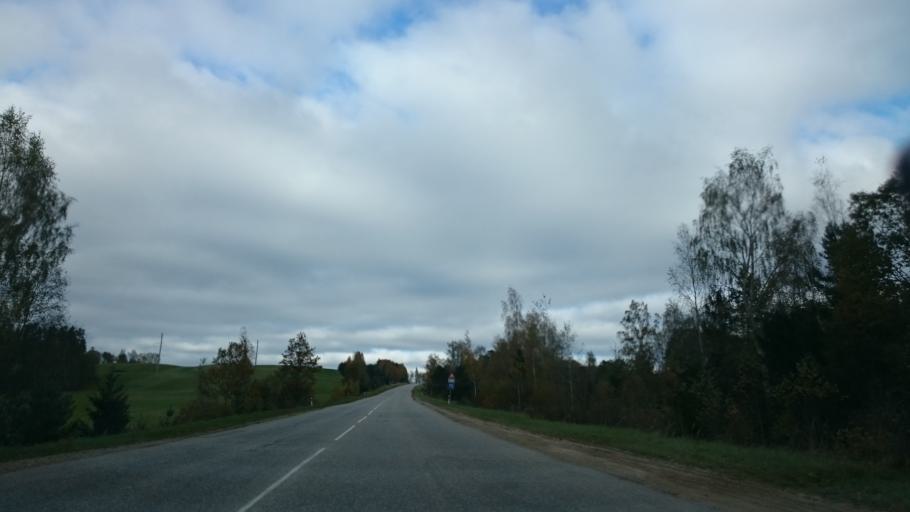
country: LV
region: Amatas Novads
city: Drabesi
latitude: 57.2612
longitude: 25.2680
